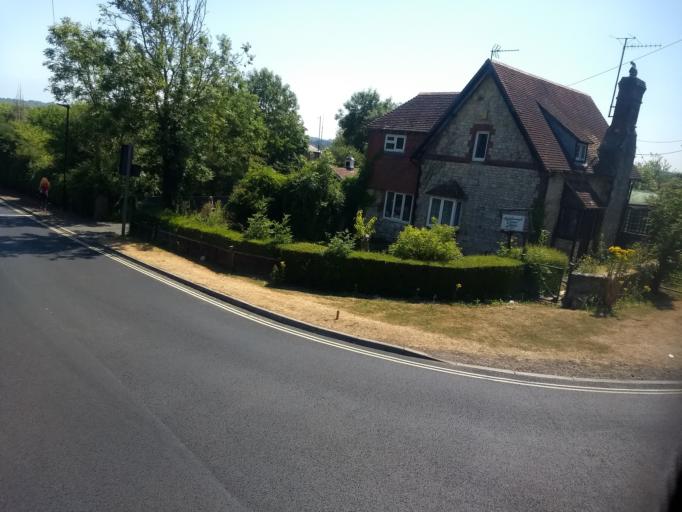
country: GB
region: England
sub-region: Isle of Wight
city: Brading
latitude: 50.6916
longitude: -1.1442
